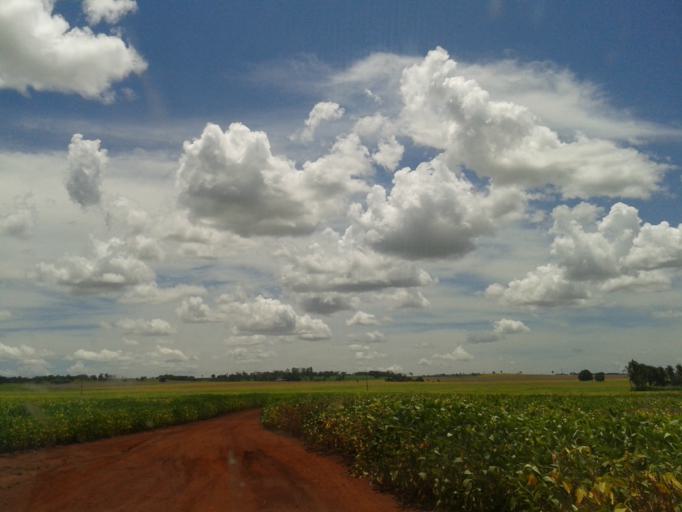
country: BR
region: Minas Gerais
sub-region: Capinopolis
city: Capinopolis
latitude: -18.7748
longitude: -49.8025
